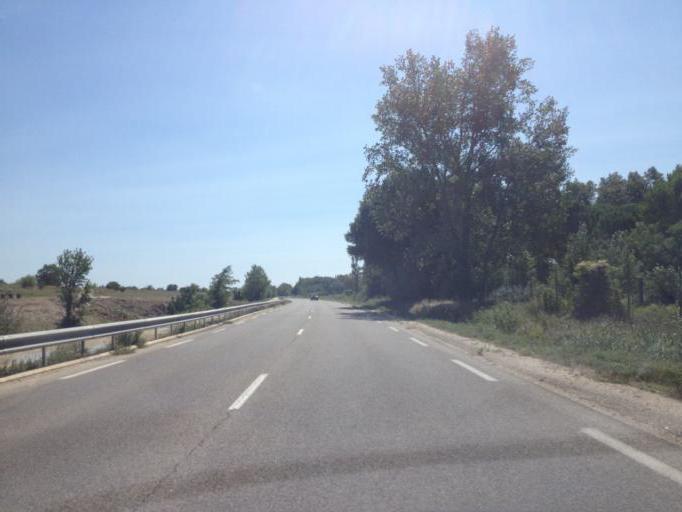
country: FR
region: Languedoc-Roussillon
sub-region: Departement du Gard
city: Roquemaure
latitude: 44.0492
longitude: 4.7868
